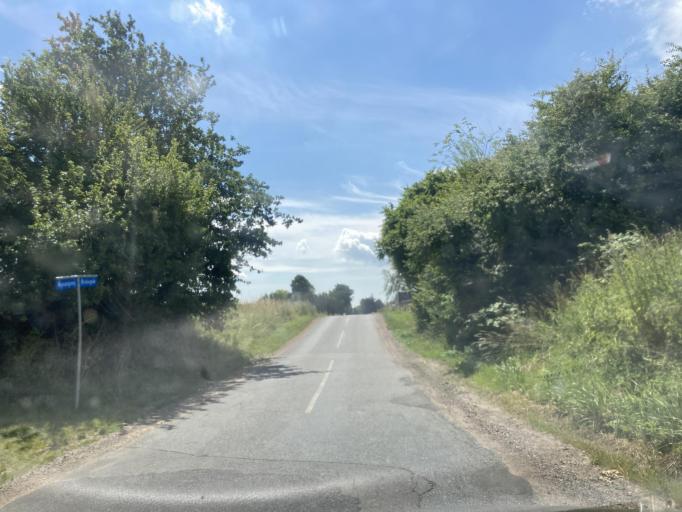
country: DK
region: Zealand
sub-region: Faxe Kommune
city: Haslev
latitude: 55.3938
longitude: 11.9399
